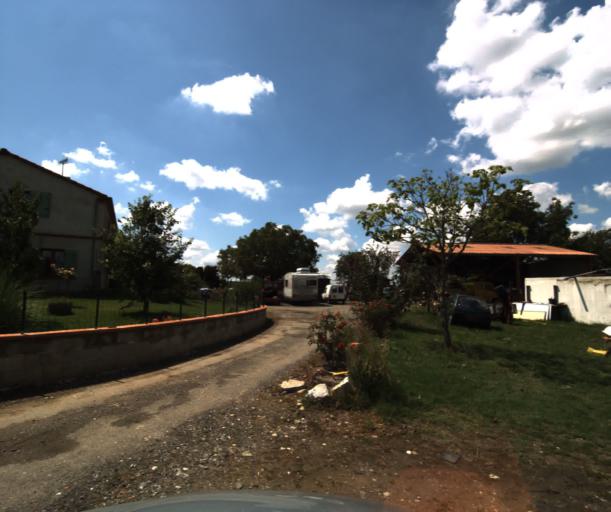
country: FR
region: Midi-Pyrenees
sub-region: Departement de la Haute-Garonne
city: Pinsaguel
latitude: 43.4965
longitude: 1.3920
